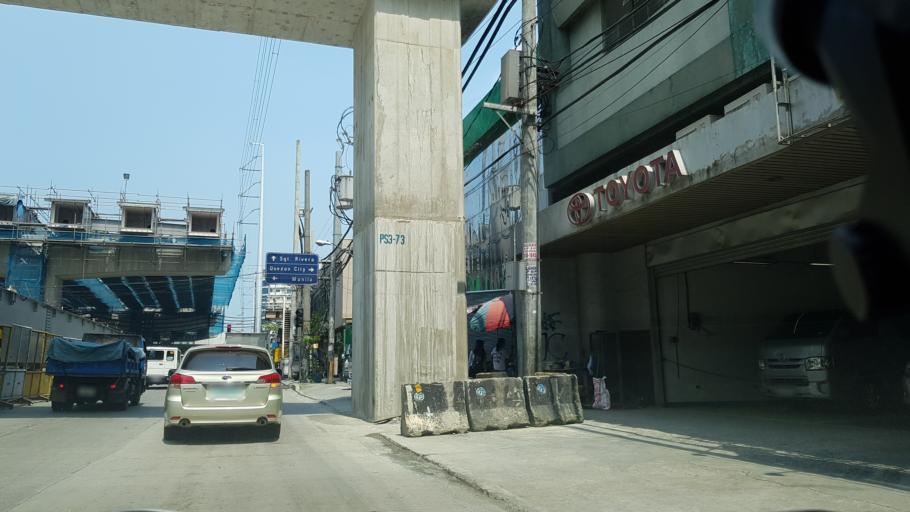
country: PH
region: Calabarzon
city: Del Monte
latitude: 14.6278
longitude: 121.0139
